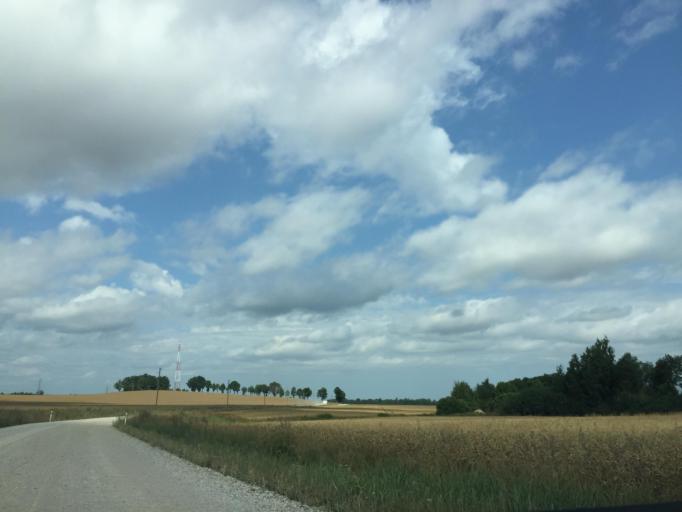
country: LV
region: Kandava
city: Kandava
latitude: 56.9737
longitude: 22.9260
